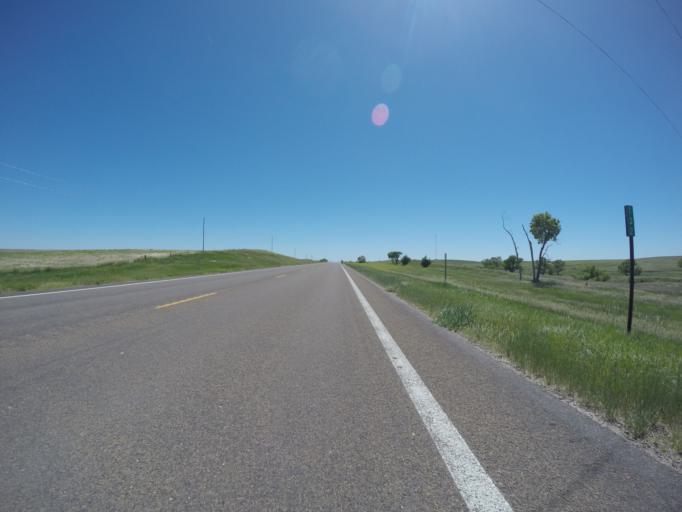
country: US
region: Kansas
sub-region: Norton County
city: Norton
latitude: 39.8285
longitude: -99.6049
